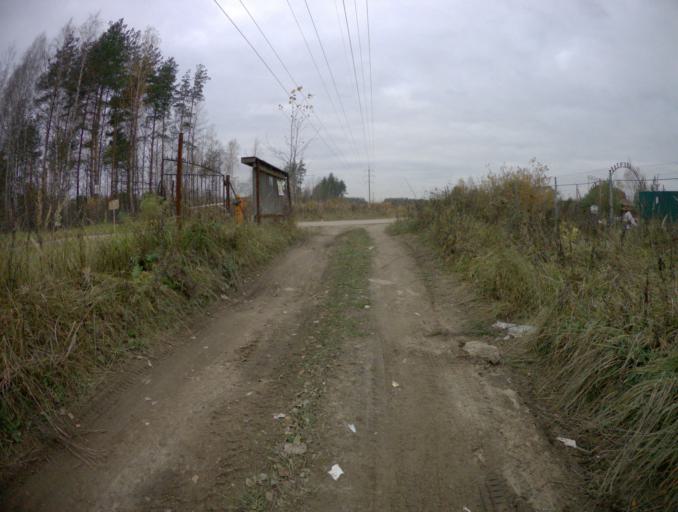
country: RU
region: Moskovskaya
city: Malaya Dubna
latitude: 55.9907
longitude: 38.9170
